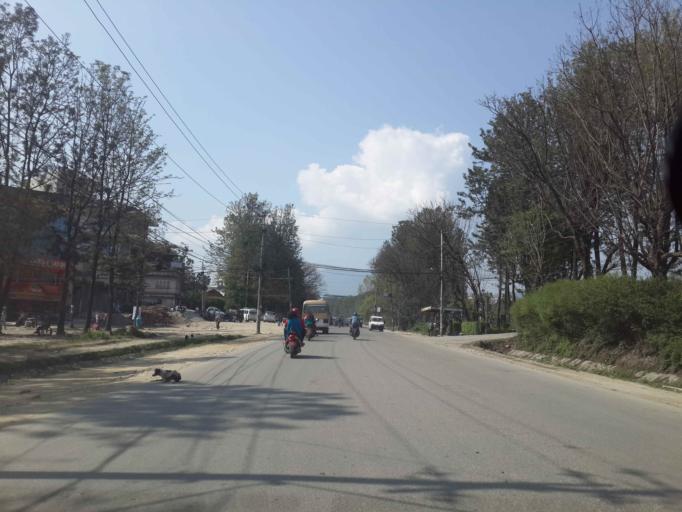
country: NP
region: Central Region
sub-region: Bagmati Zone
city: Kathmandu
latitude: 27.7341
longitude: 85.3429
